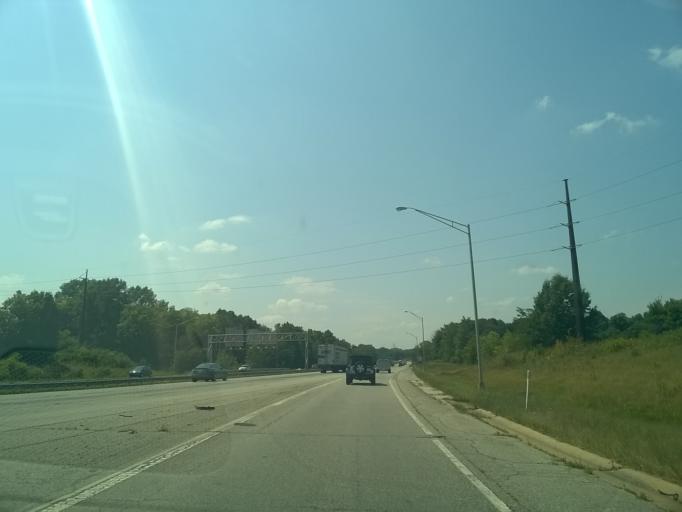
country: US
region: Indiana
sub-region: Hendricks County
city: Plainfield
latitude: 39.6660
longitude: -86.3764
